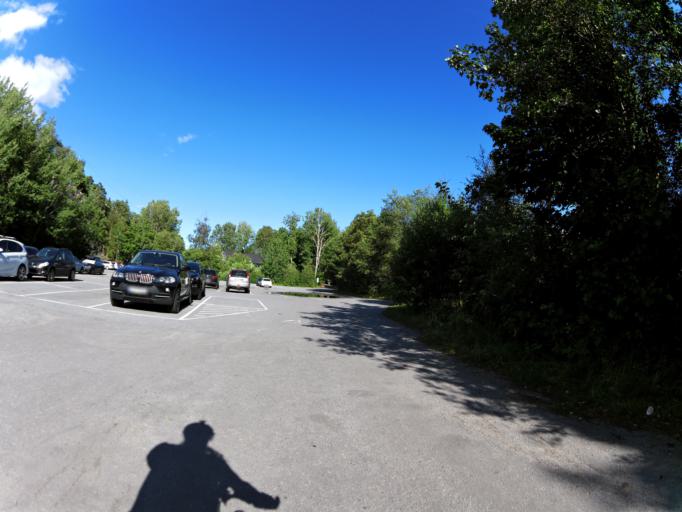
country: NO
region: Ostfold
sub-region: Fredrikstad
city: Fredrikstad
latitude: 59.1711
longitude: 10.8312
